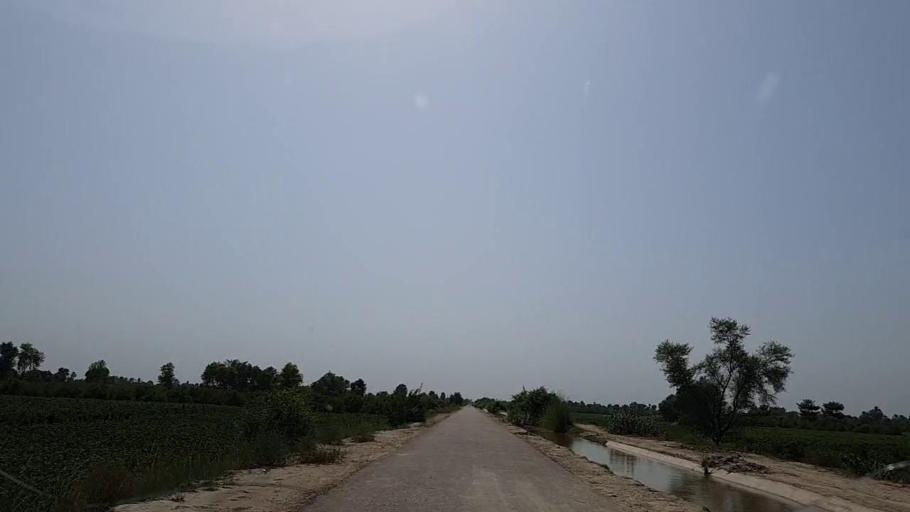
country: PK
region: Sindh
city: Kandiaro
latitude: 27.0504
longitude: 68.1616
